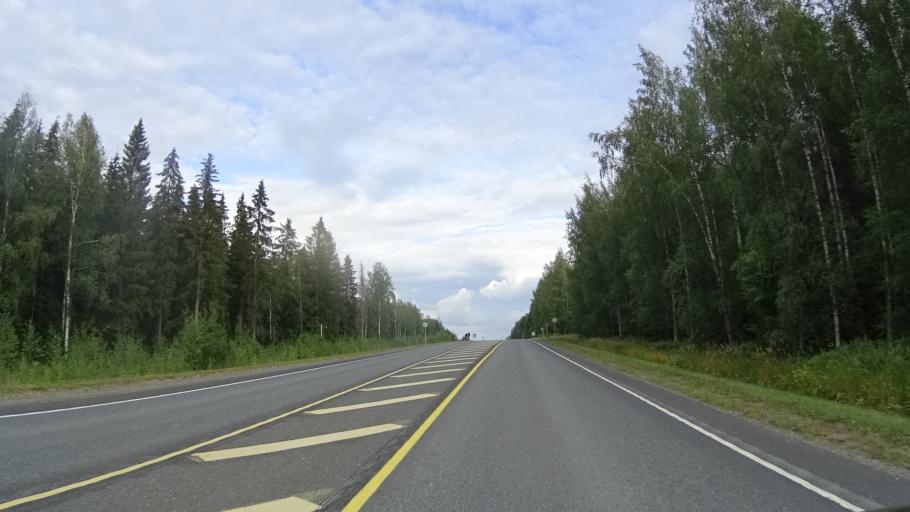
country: FI
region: Haeme
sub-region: Haemeenlinna
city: Parola
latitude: 61.0259
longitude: 24.3033
